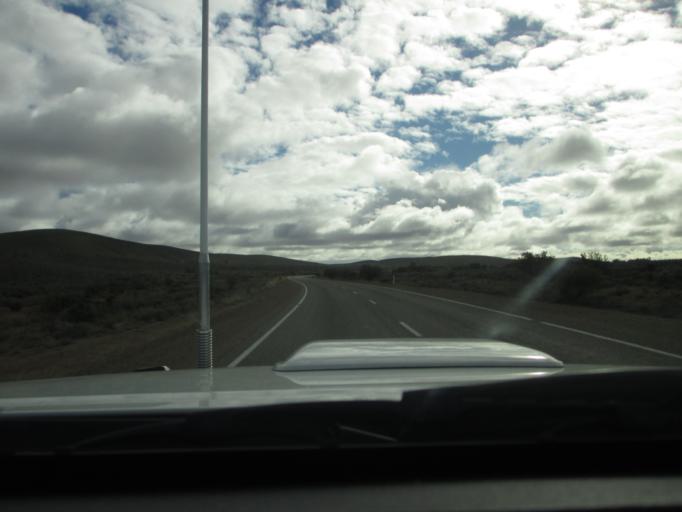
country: AU
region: South Australia
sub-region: Flinders Ranges
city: Quorn
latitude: -32.2162
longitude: 138.5191
